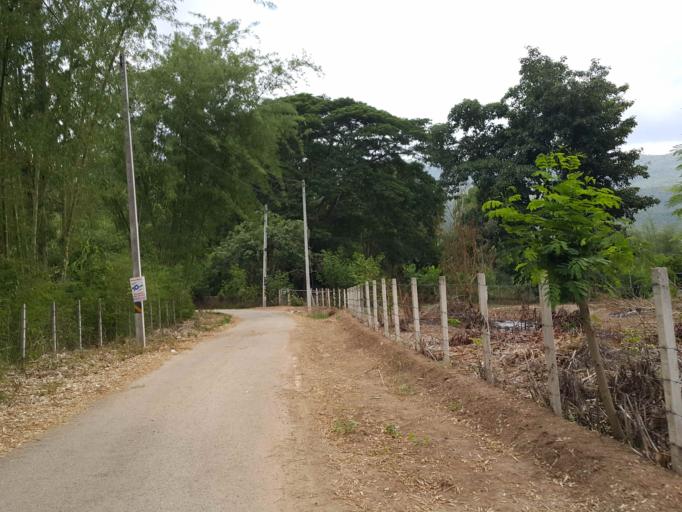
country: TH
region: Chiang Mai
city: Hang Dong
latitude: 18.7559
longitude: 98.9035
